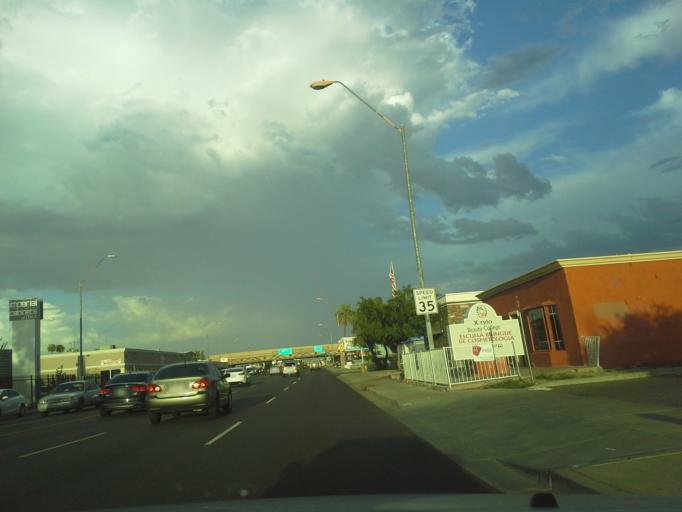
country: US
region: Arizona
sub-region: Maricopa County
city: Phoenix
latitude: 33.4656
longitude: -112.0412
